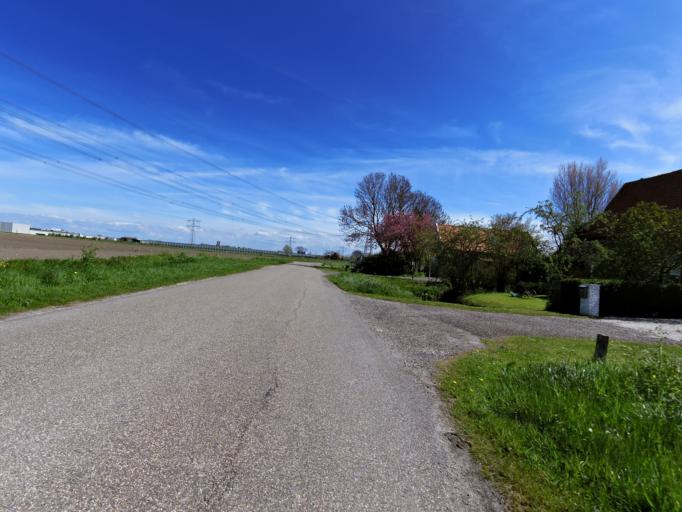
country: NL
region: South Holland
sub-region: Gemeente Brielle
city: Brielle
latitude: 51.9077
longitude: 4.1293
